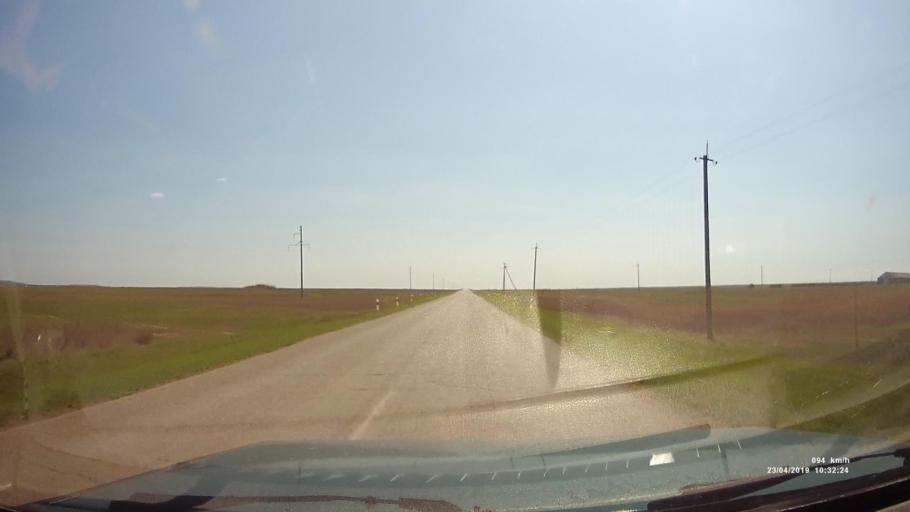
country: RU
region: Kalmykiya
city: Yashalta
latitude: 46.5804
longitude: 42.5773
